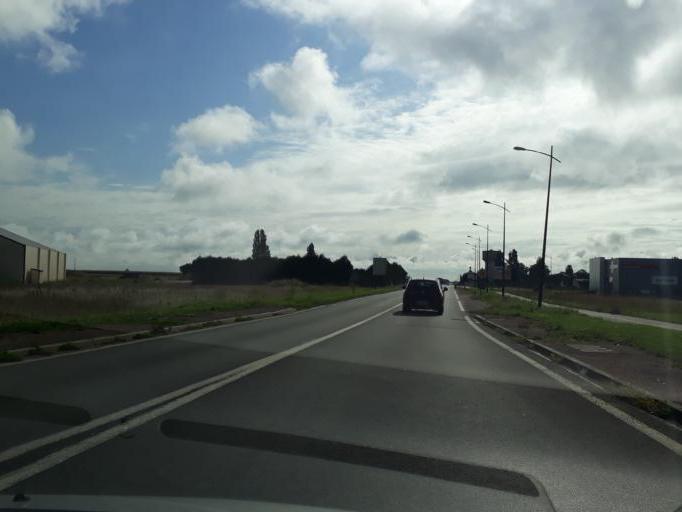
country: FR
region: Centre
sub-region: Departement d'Eure-et-Loir
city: Chateaudun
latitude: 48.0689
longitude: 1.3626
